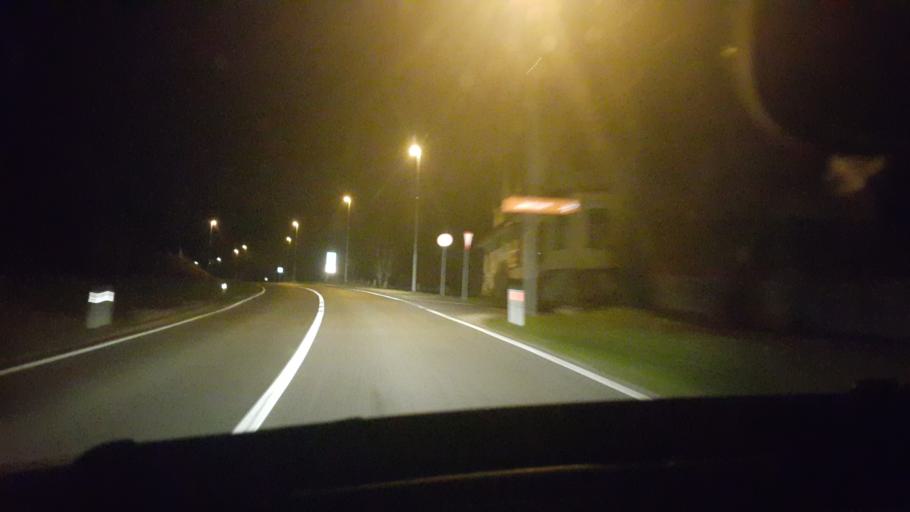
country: SI
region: Selnica ob Dravi
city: Selnica ob Dravi
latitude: 46.5570
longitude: 15.4587
